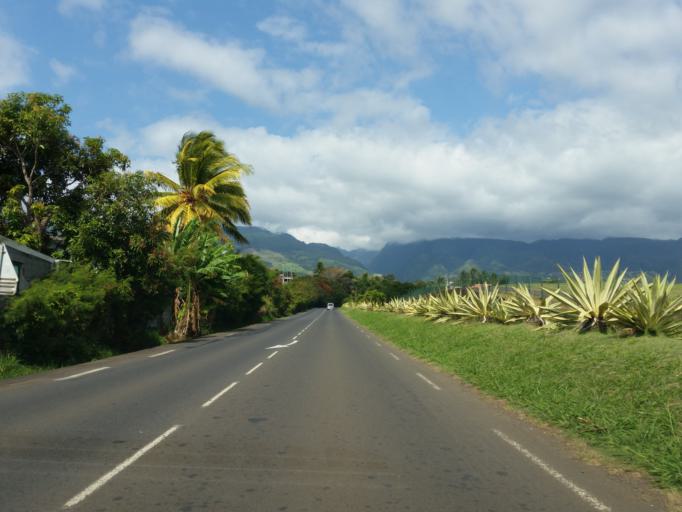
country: RE
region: Reunion
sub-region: Reunion
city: Sainte-Marie
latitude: -20.8949
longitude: 55.5306
